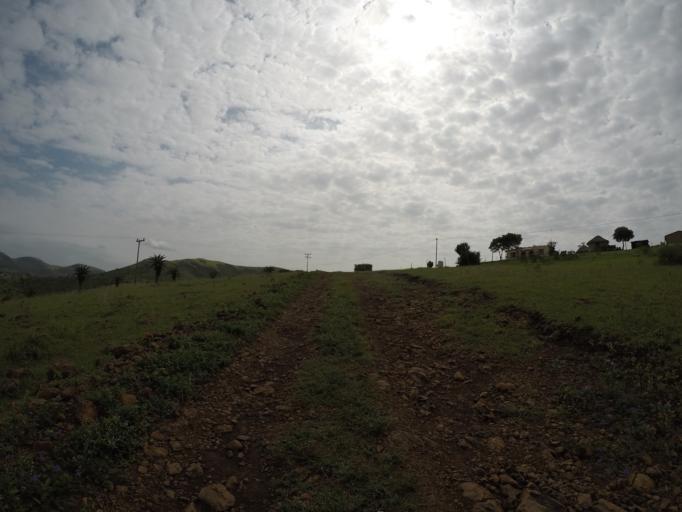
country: ZA
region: KwaZulu-Natal
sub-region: uThungulu District Municipality
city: Empangeni
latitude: -28.6178
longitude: 31.8946
